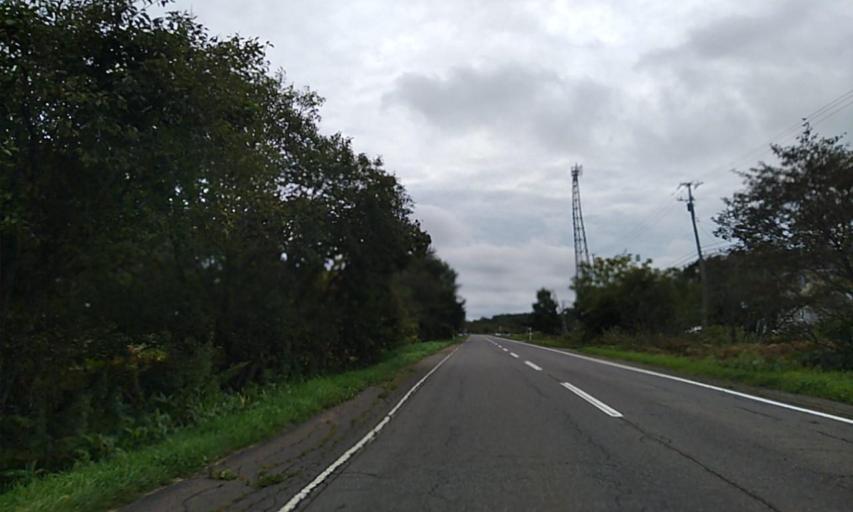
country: JP
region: Hokkaido
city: Shibetsu
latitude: 43.5453
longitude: 145.2297
